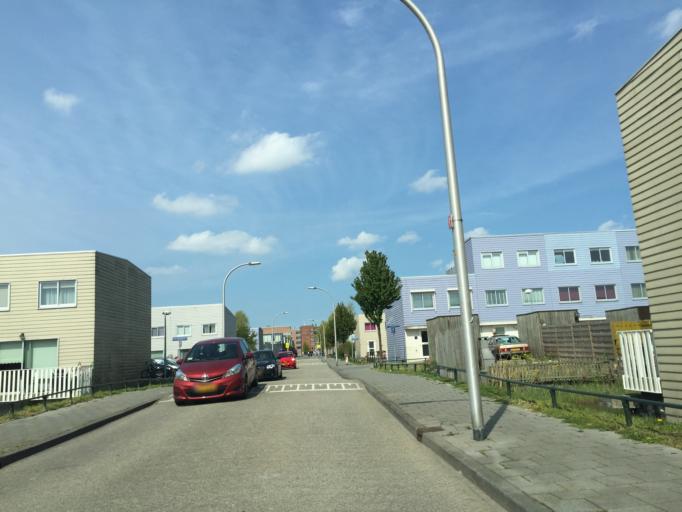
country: NL
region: South Holland
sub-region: Gemeente Den Haag
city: Ypenburg
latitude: 52.0363
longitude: 4.3728
